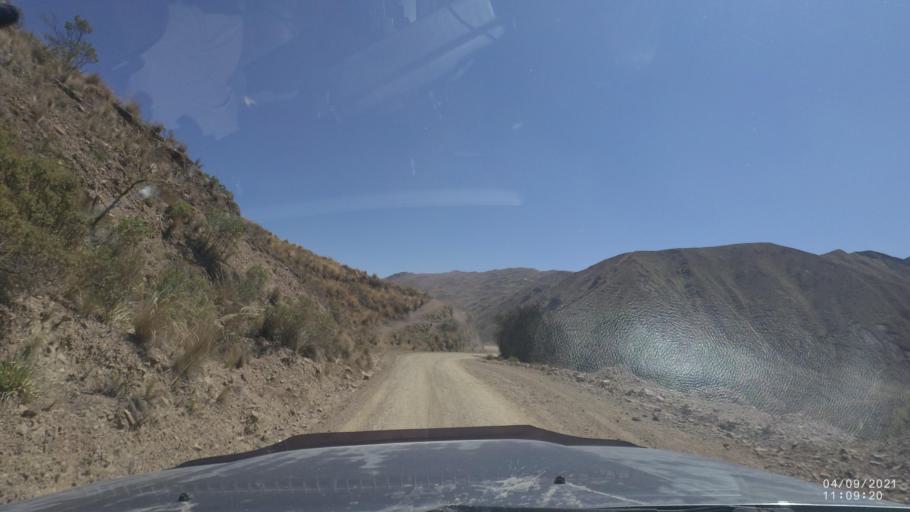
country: BO
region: Cochabamba
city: Sipe Sipe
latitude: -17.2797
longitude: -66.4785
